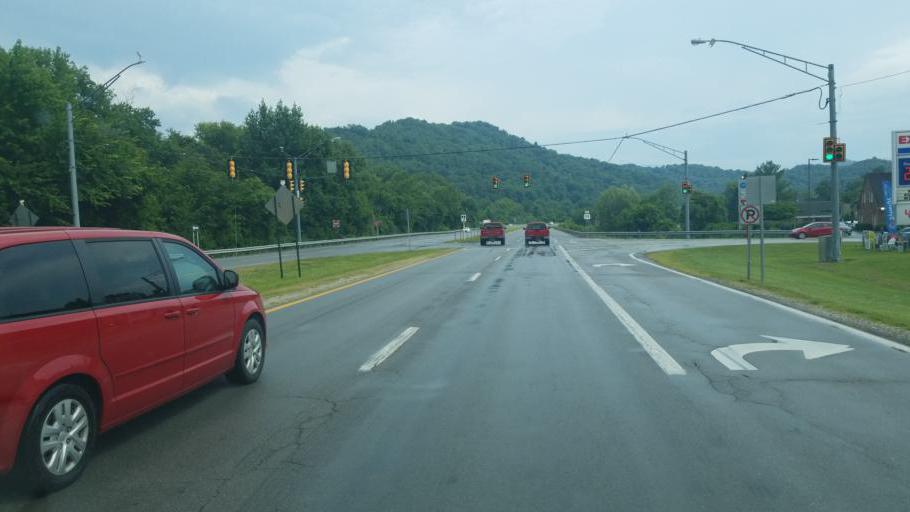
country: US
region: West Virginia
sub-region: Logan County
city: Chapmanville
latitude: 37.9597
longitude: -82.0198
